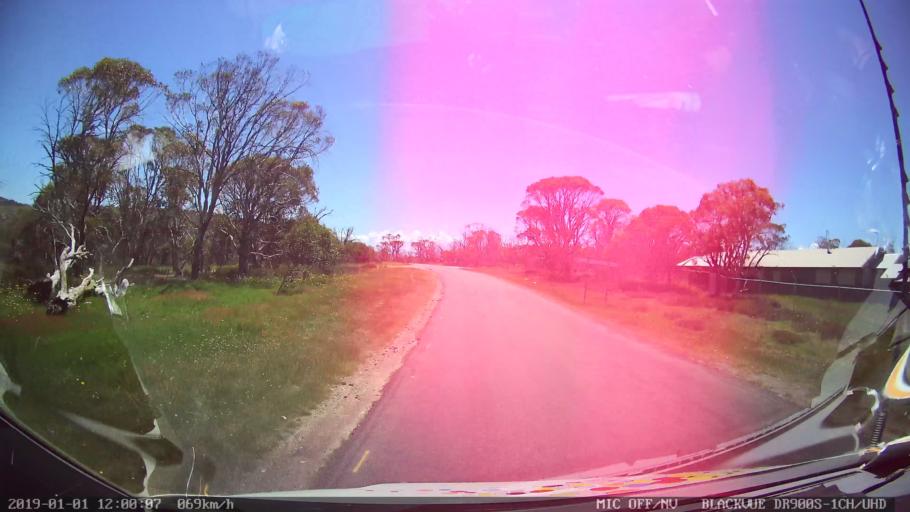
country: AU
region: New South Wales
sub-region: Snowy River
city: Jindabyne
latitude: -35.8874
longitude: 148.4574
